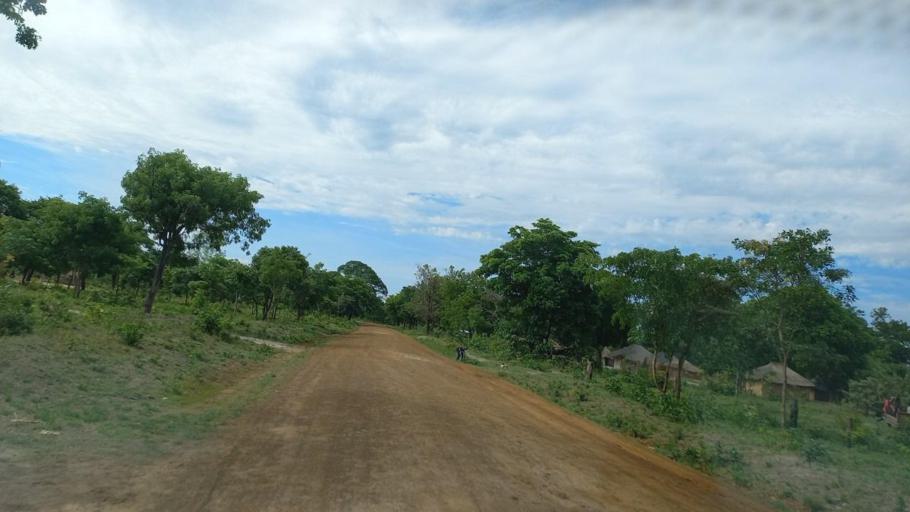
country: ZM
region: North-Western
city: Kabompo
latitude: -13.4583
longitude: 24.4271
